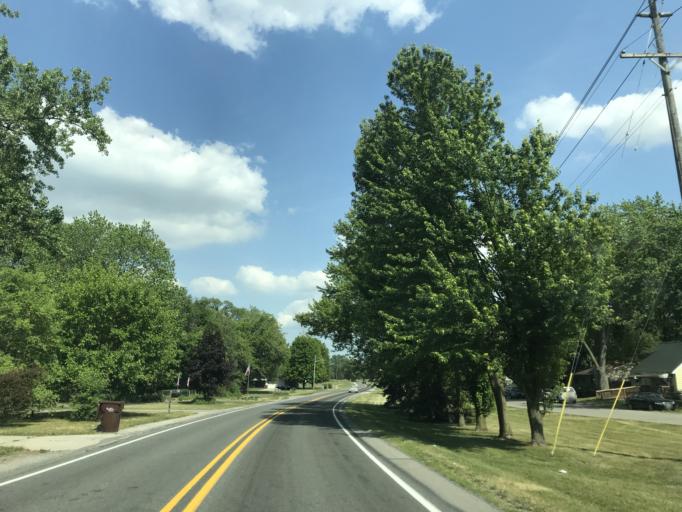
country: US
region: Michigan
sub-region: Washtenaw County
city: Ypsilanti
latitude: 42.2612
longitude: -83.5895
